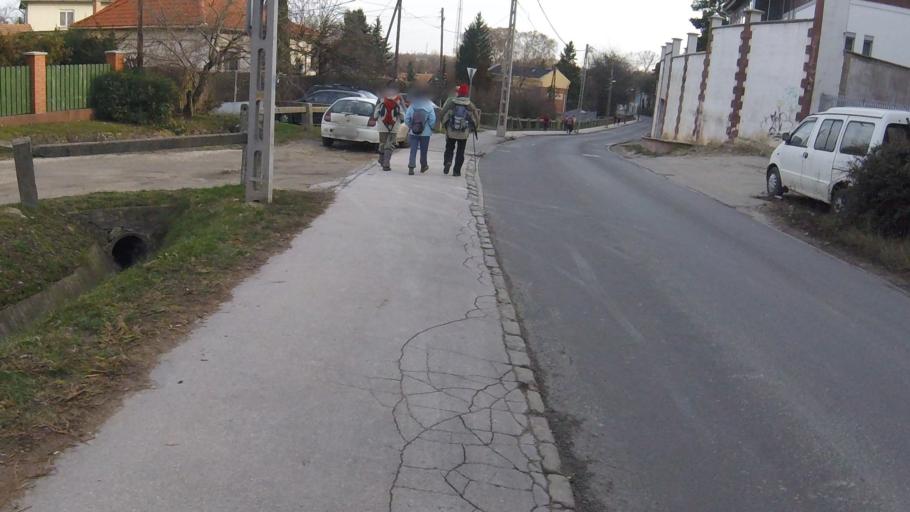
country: HU
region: Pest
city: Urom
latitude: 47.5883
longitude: 19.0409
